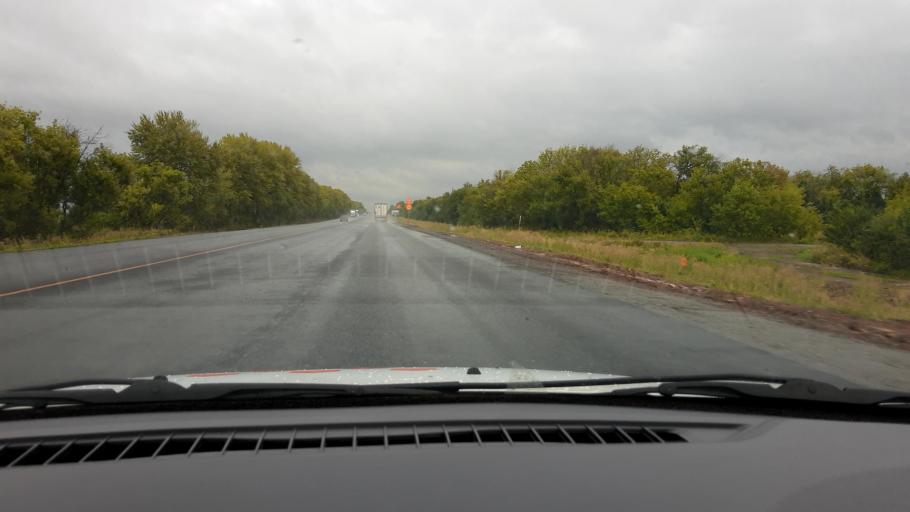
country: RU
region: Chuvashia
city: Yantikovo
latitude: 55.7990
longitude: 47.8509
